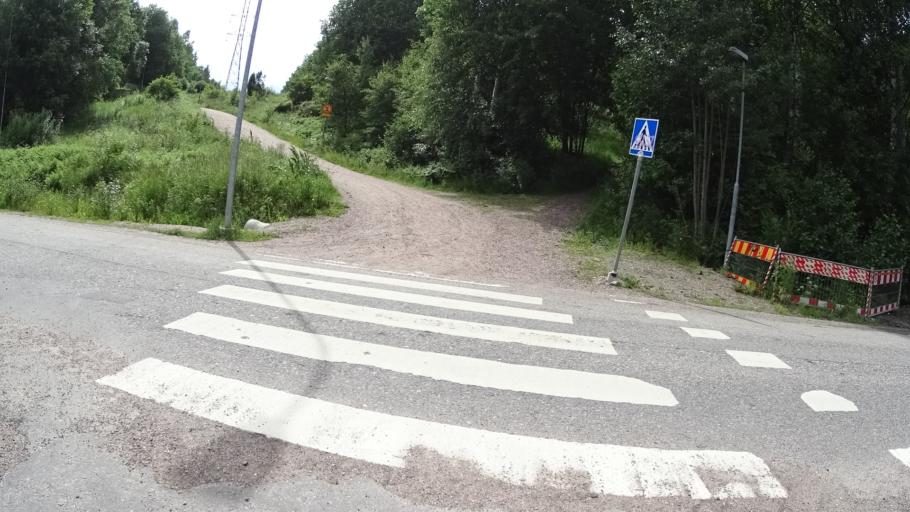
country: FI
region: Uusimaa
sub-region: Helsinki
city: Teekkarikylae
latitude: 60.2541
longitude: 24.8468
